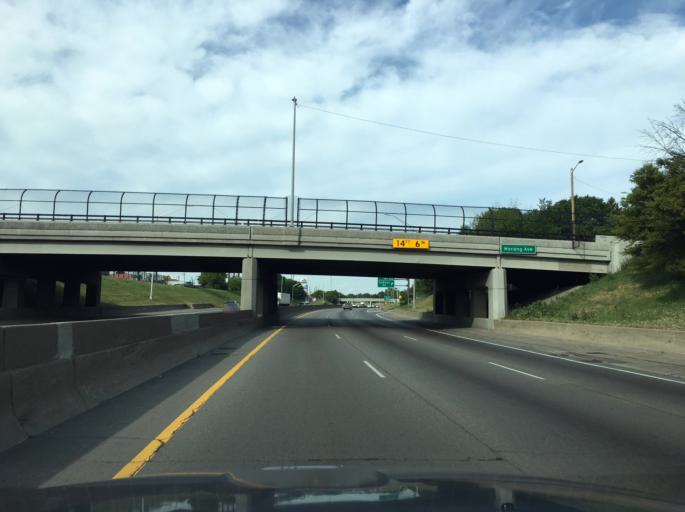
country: US
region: Michigan
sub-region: Wayne County
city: Harper Woods
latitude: 42.4197
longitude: -82.9331
